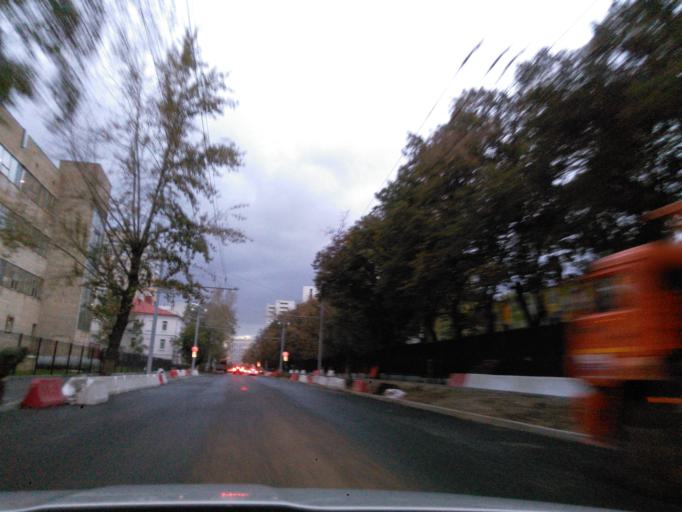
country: RU
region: Moscow
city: Zamoskvorech'ye
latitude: 55.7244
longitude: 37.6163
